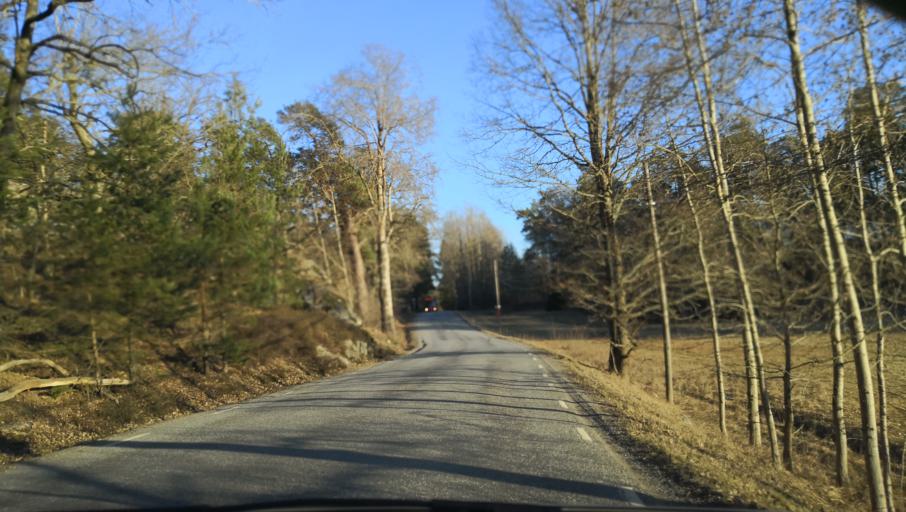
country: SE
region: Stockholm
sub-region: Varmdo Kommun
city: Gustavsberg
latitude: 59.3300
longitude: 18.4099
